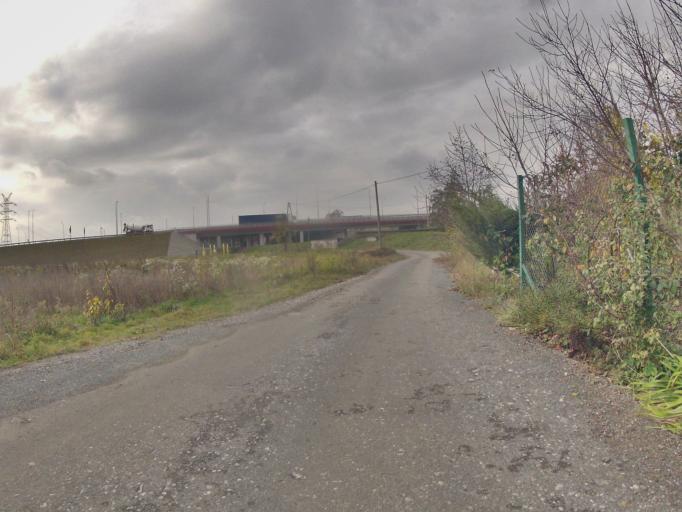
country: PL
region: Lesser Poland Voivodeship
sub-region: Powiat wielicki
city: Kokotow
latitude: 50.0628
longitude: 20.0766
